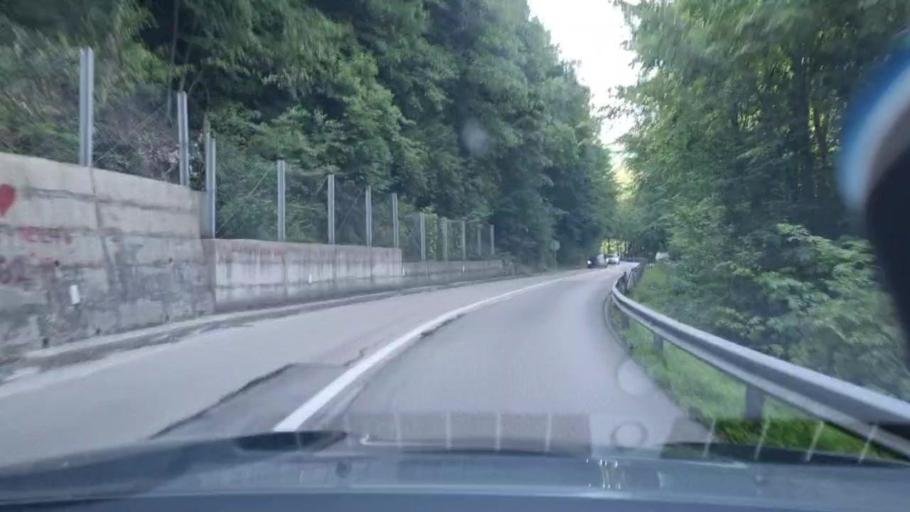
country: BA
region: Federation of Bosnia and Herzegovina
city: Bosanska Krupa
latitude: 44.8728
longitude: 16.0784
